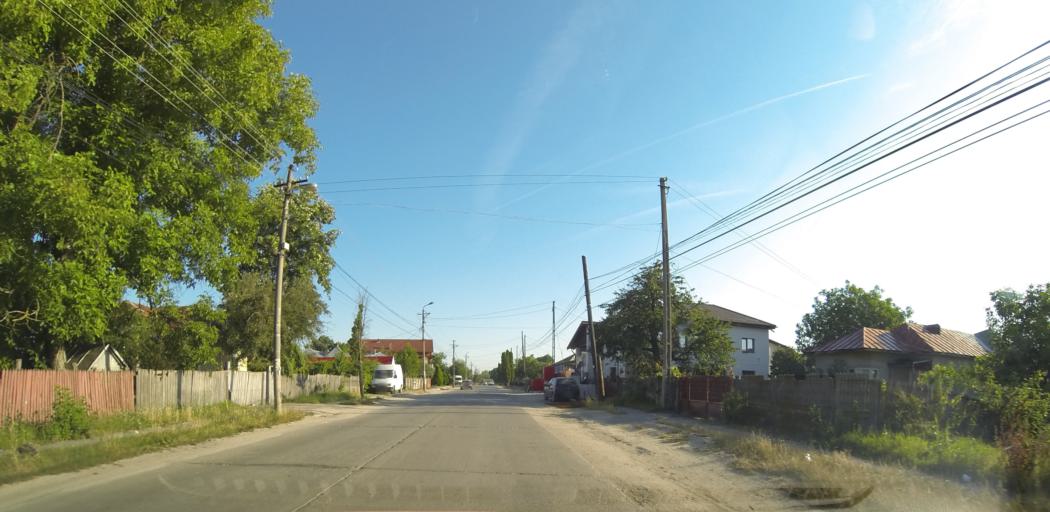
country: RO
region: Valcea
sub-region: Comuna Balcesti
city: Balcesti
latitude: 44.6243
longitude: 23.9417
